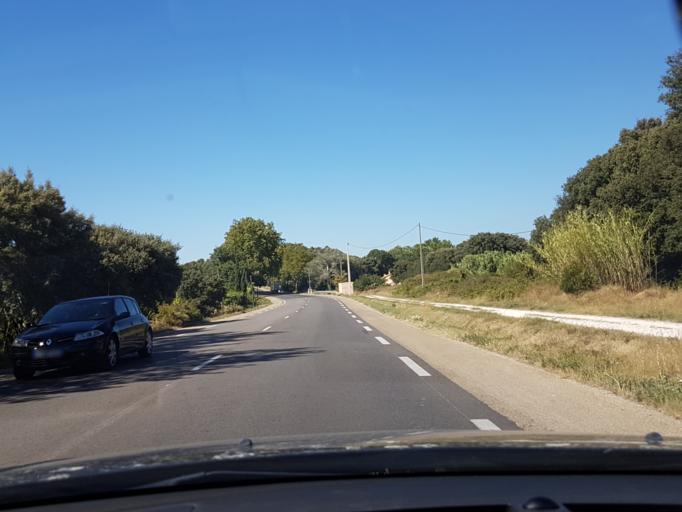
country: FR
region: Provence-Alpes-Cote d'Azur
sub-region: Departement des Bouches-du-Rhone
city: Orgon
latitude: 43.8026
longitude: 5.0268
